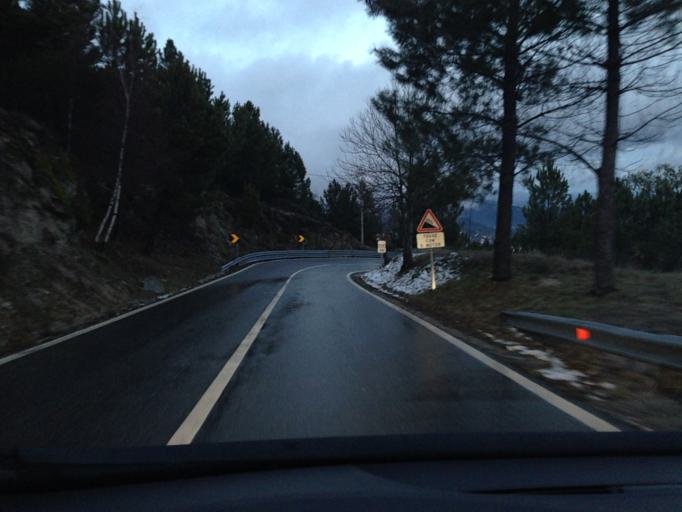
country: PT
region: Castelo Branco
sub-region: Covilha
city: Covilha
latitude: 40.2848
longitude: -7.5208
